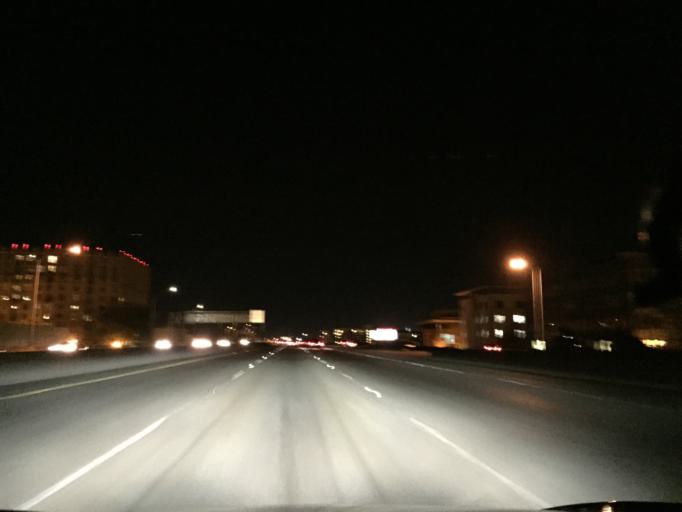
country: US
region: California
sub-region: Alameda County
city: Oakland
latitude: 37.7992
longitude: -122.2770
